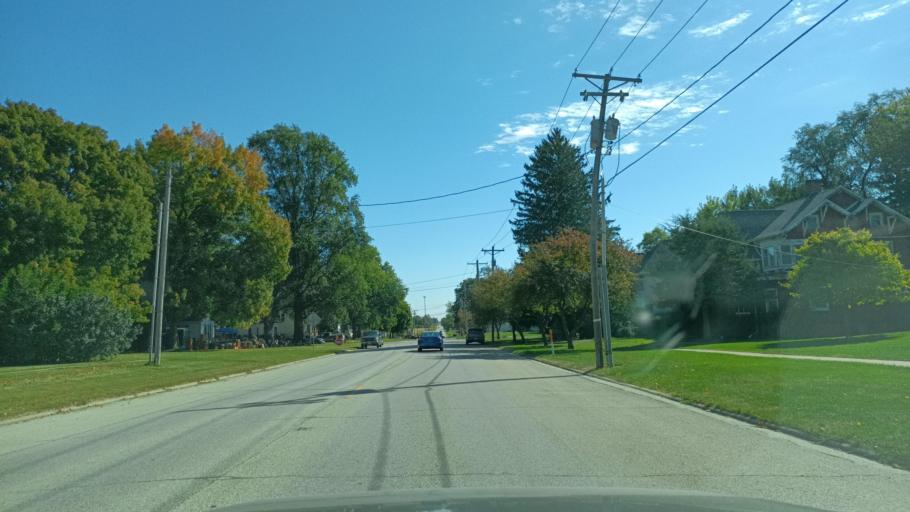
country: US
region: Illinois
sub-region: Knox County
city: Knoxville
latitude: 40.9079
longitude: -90.2726
